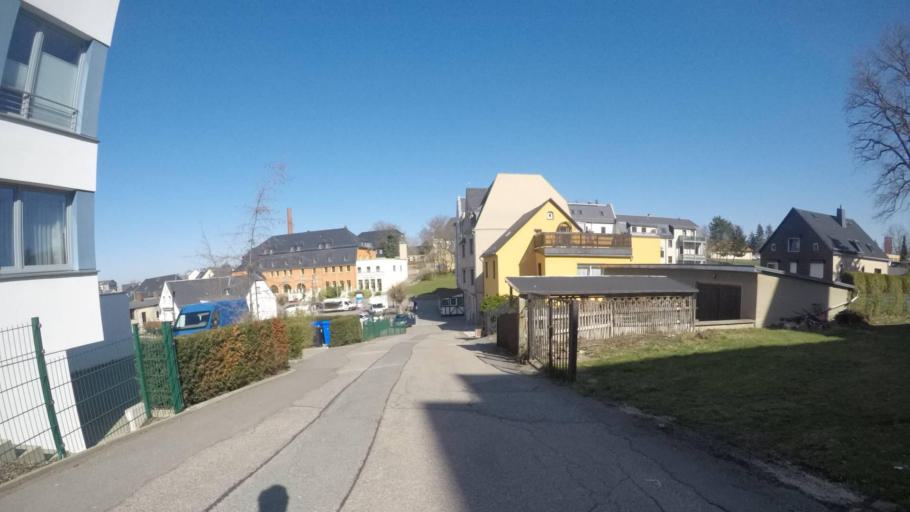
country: DE
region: Saxony
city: Limbach-Oberfrohna
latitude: 50.8567
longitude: 12.7673
